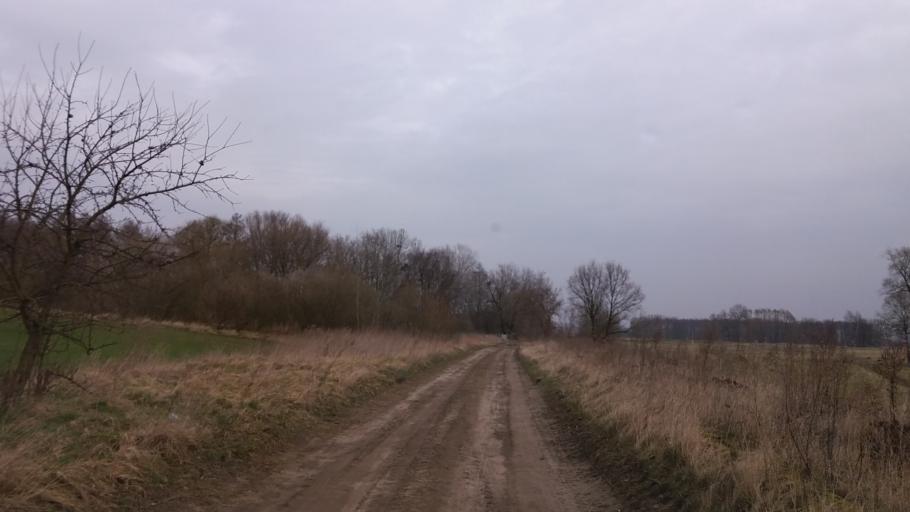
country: PL
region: West Pomeranian Voivodeship
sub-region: Powiat choszczenski
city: Pelczyce
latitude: 53.1114
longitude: 15.3374
